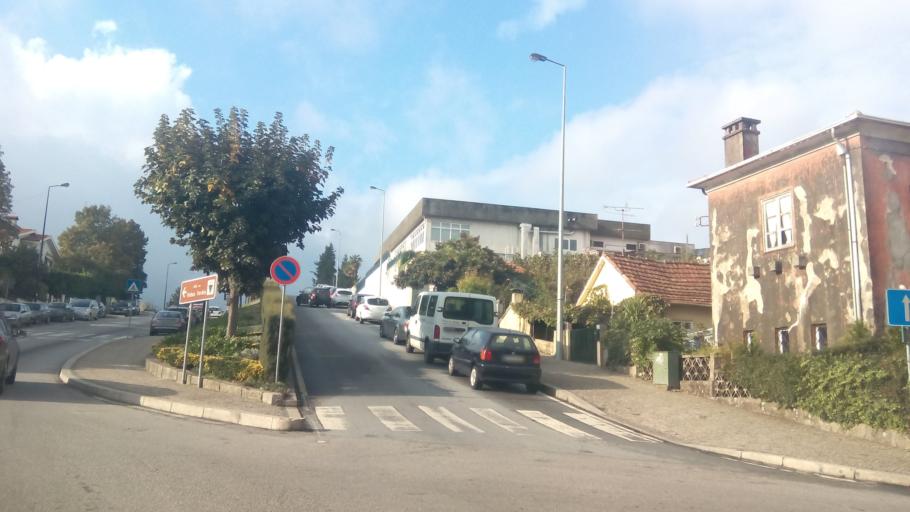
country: PT
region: Porto
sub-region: Paredes
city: Paredes
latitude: 41.2032
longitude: -8.3309
